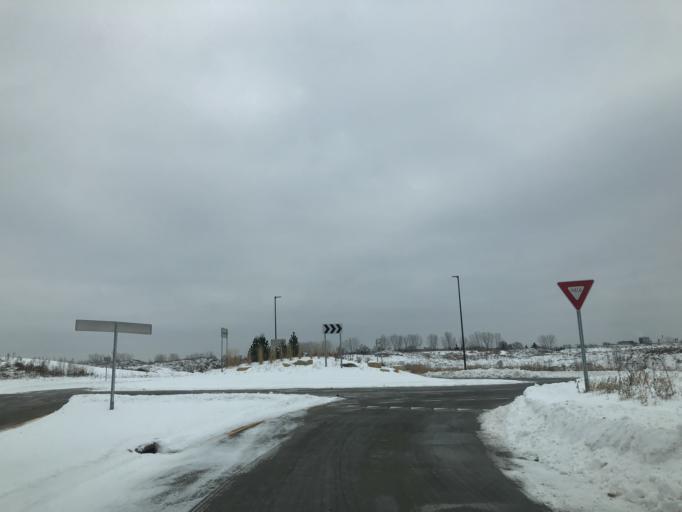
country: US
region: Minnesota
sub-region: Hennepin County
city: Osseo
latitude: 45.0919
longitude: -93.4126
